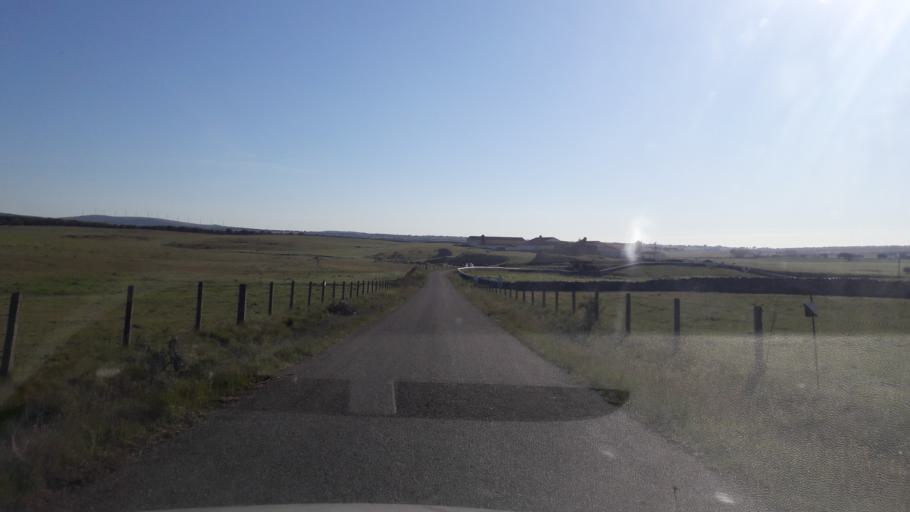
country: ES
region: Castille and Leon
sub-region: Provincia de Salamanca
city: Endrinal
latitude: 40.6108
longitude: -5.8261
